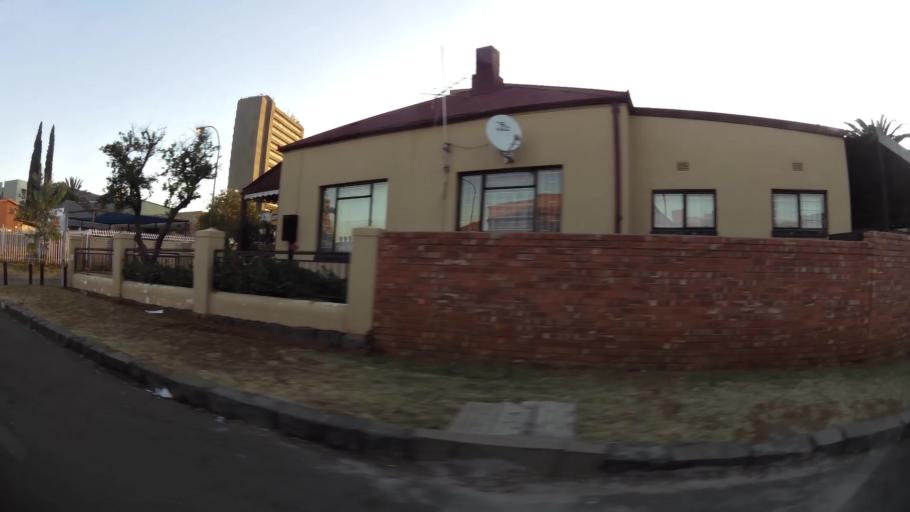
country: ZA
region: Northern Cape
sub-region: Frances Baard District Municipality
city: Kimberley
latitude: -28.7368
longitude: 24.7671
